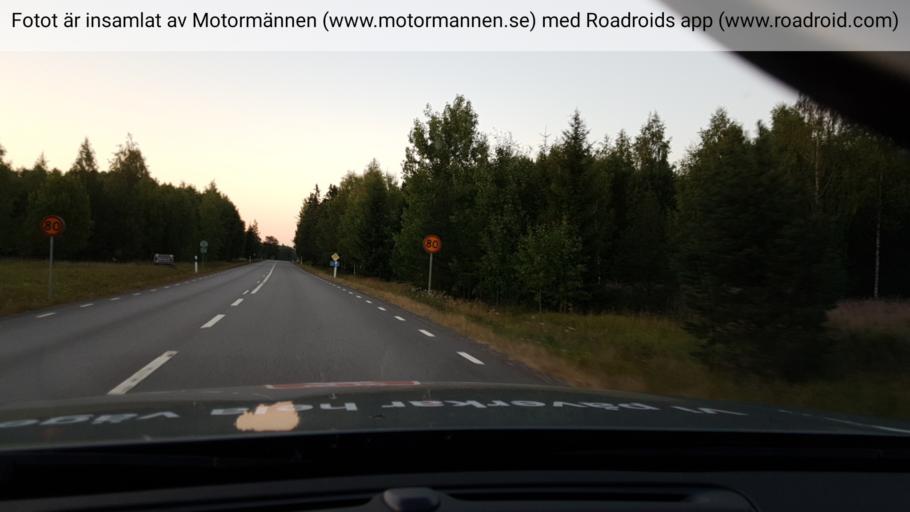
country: SE
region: Uppsala
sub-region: Heby Kommun
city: OEstervala
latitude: 60.1082
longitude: 17.2065
